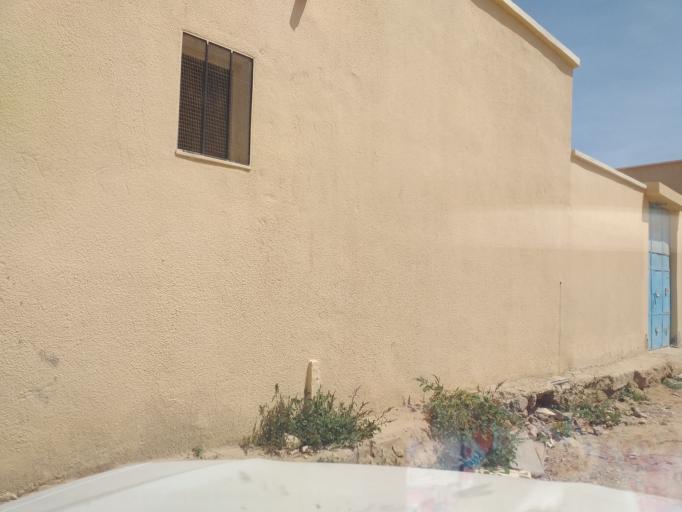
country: TN
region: Qabis
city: Gabes
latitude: 33.9423
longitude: 10.0704
